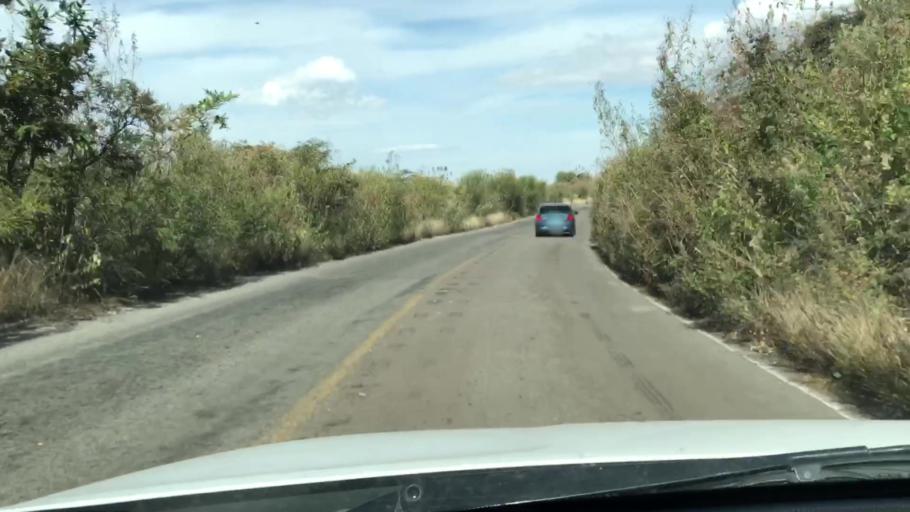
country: MX
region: Jalisco
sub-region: Zacoalco de Torres
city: Barranca de Otates (Barranca de Otatan)
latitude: 20.2276
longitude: -103.6892
